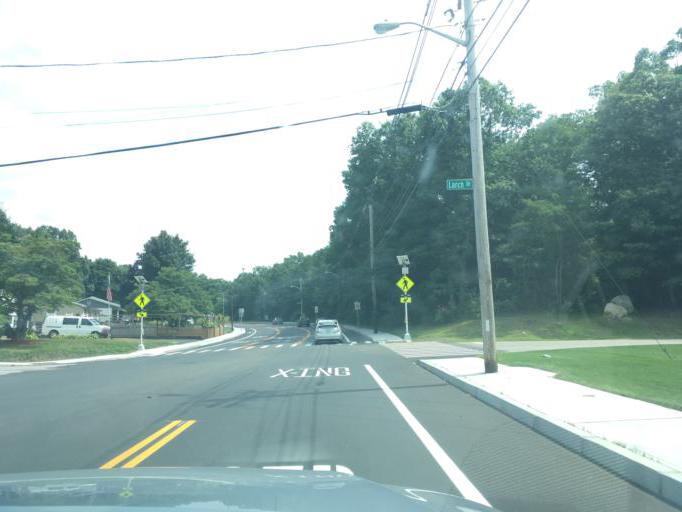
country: US
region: Rhode Island
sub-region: Kent County
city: West Warwick
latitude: 41.6690
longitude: -71.5518
